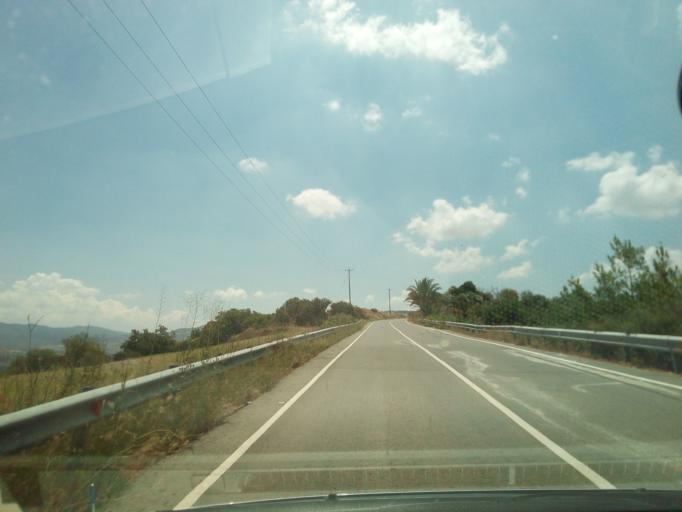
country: CY
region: Pafos
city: Polis
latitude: 34.9571
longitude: 32.4795
